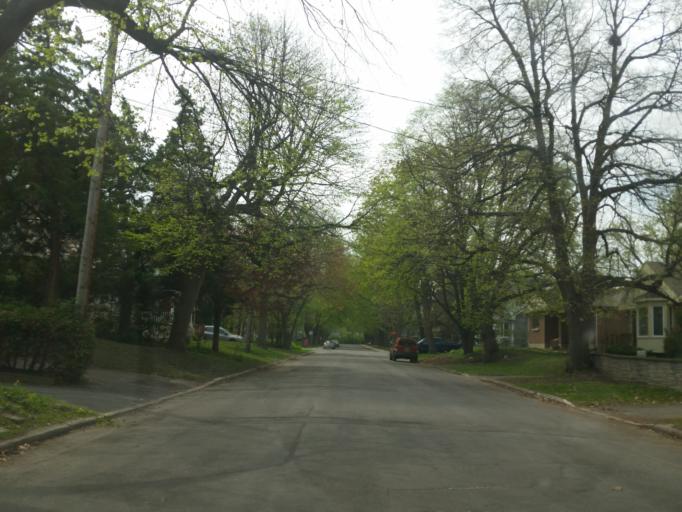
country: CA
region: Ontario
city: Ottawa
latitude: 45.4021
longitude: -75.7469
